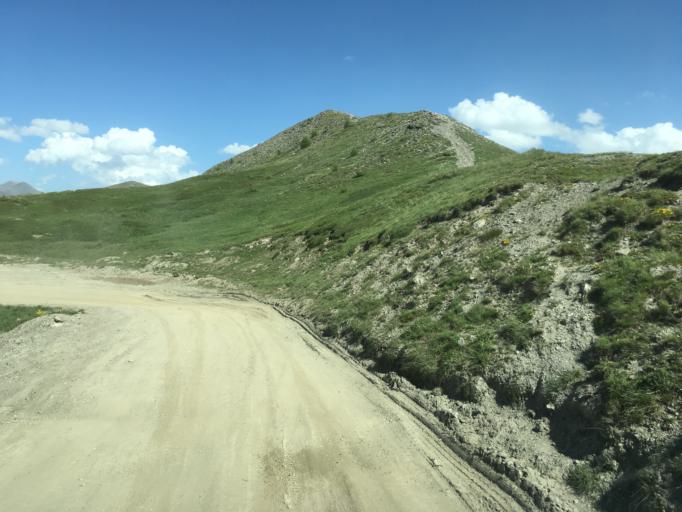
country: IT
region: Piedmont
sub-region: Provincia di Torino
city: Sestriere
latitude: 44.9856
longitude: 6.8718
